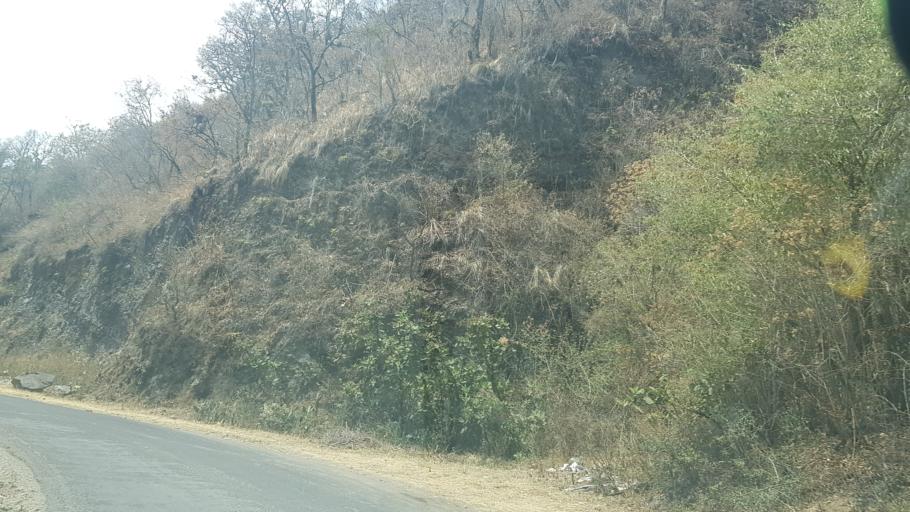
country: MX
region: Puebla
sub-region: Tochimilco
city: La Magdalena Yancuitlalpan
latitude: 18.8768
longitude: -98.6110
